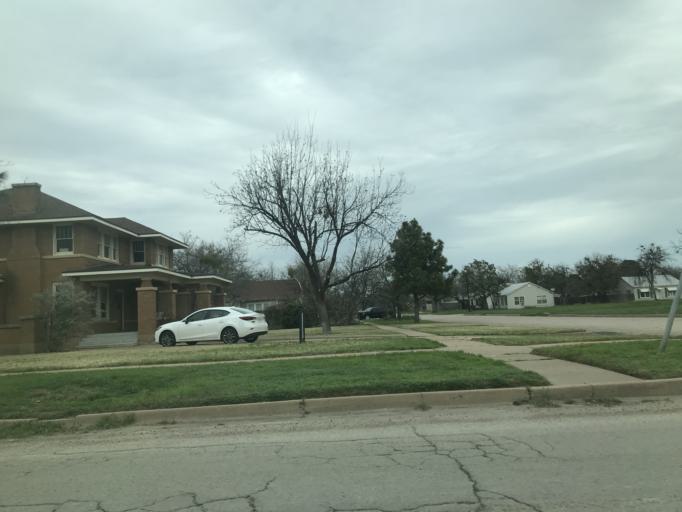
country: US
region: Texas
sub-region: Taylor County
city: Abilene
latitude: 32.4579
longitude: -99.7400
